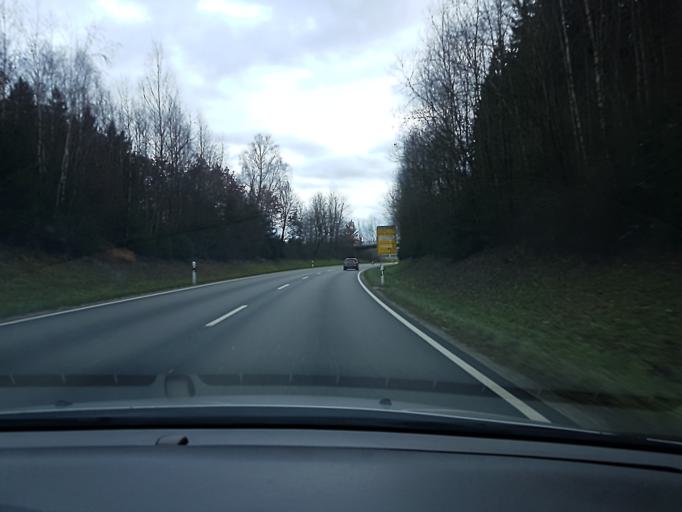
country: DE
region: Bavaria
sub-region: Lower Bavaria
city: Vilsbiburg
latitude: 48.4497
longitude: 12.3361
